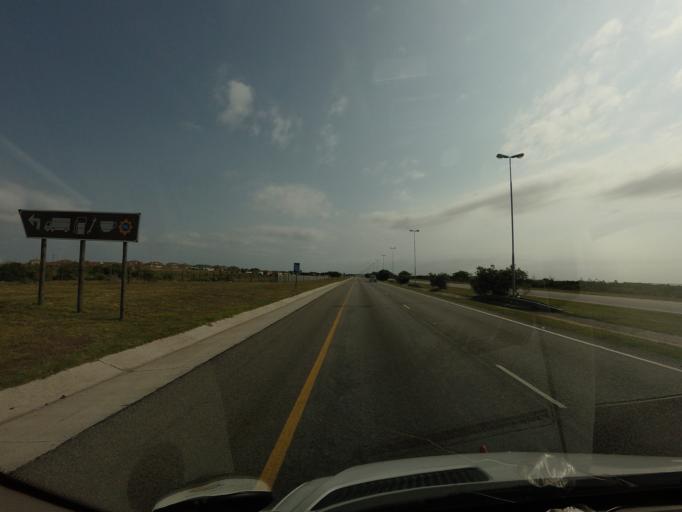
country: ZA
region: Eastern Cape
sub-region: Nelson Mandela Bay Metropolitan Municipality
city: Port Elizabeth
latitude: -33.8302
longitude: 25.6440
